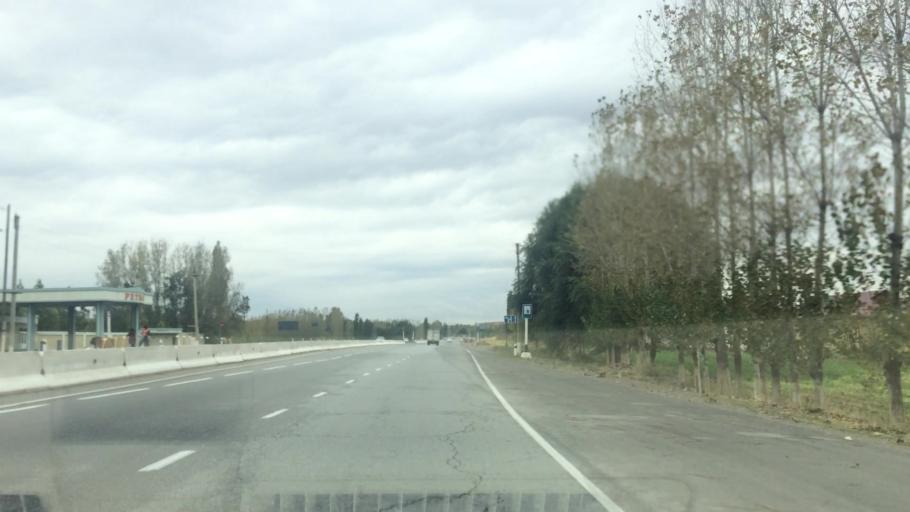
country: UZ
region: Jizzax
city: Jizzax
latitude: 39.9622
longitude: 67.5481
